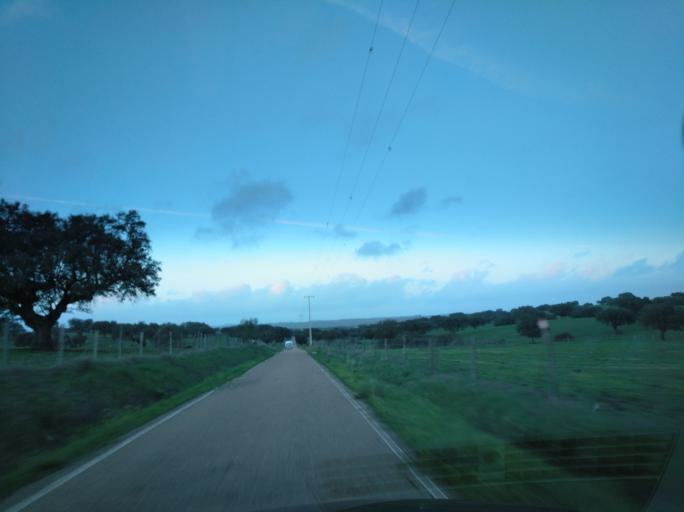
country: PT
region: Portalegre
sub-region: Campo Maior
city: Campo Maior
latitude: 39.0770
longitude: -7.1162
